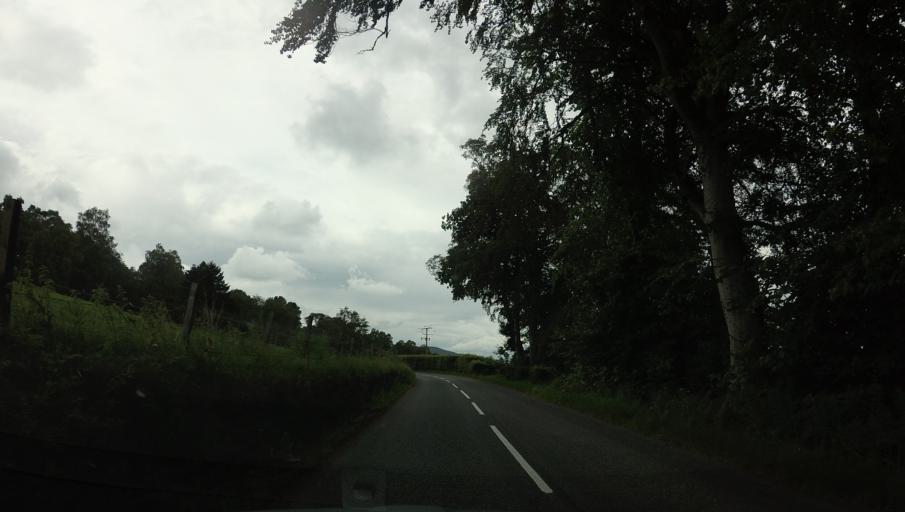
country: GB
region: Scotland
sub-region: Aberdeenshire
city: Aboyne
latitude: 57.0616
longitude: -2.7008
